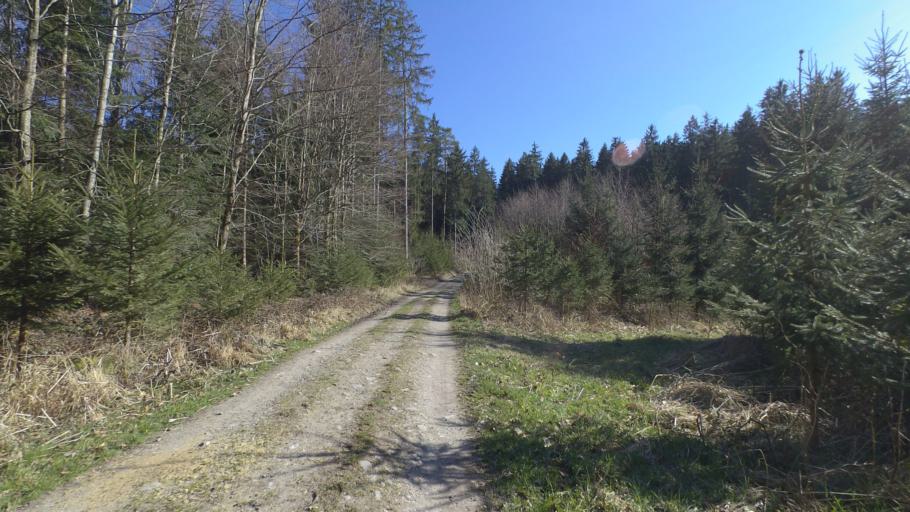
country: DE
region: Bavaria
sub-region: Upper Bavaria
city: Chieming
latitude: 47.9473
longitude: 12.5223
